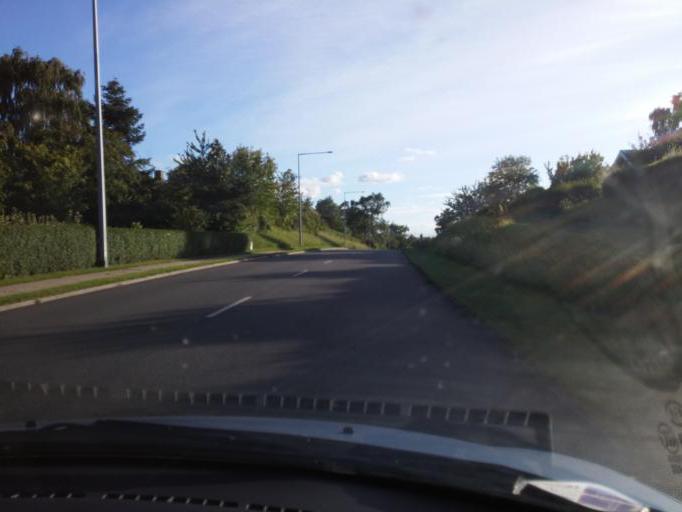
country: DK
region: South Denmark
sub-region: Kerteminde Kommune
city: Munkebo
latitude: 55.4508
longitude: 10.5483
